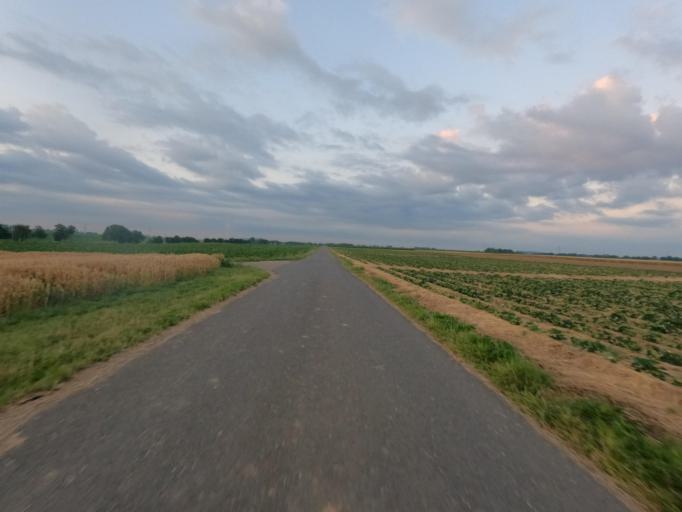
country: DE
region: North Rhine-Westphalia
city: Baesweiler
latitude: 50.9740
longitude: 6.1897
